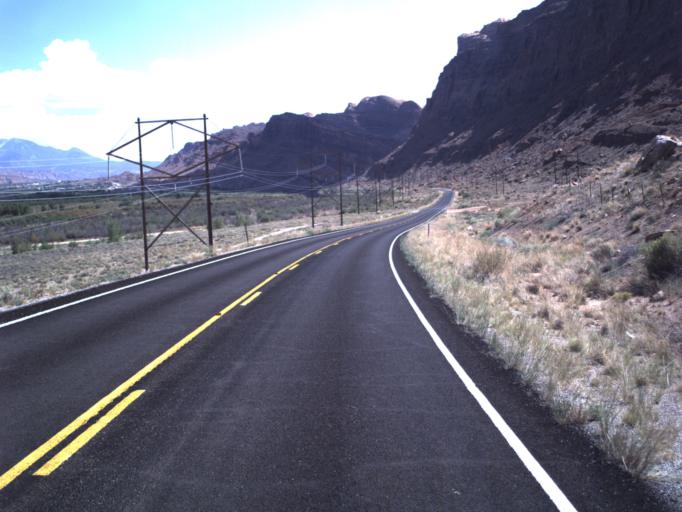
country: US
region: Utah
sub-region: Grand County
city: Moab
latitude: 38.5938
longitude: -109.5965
